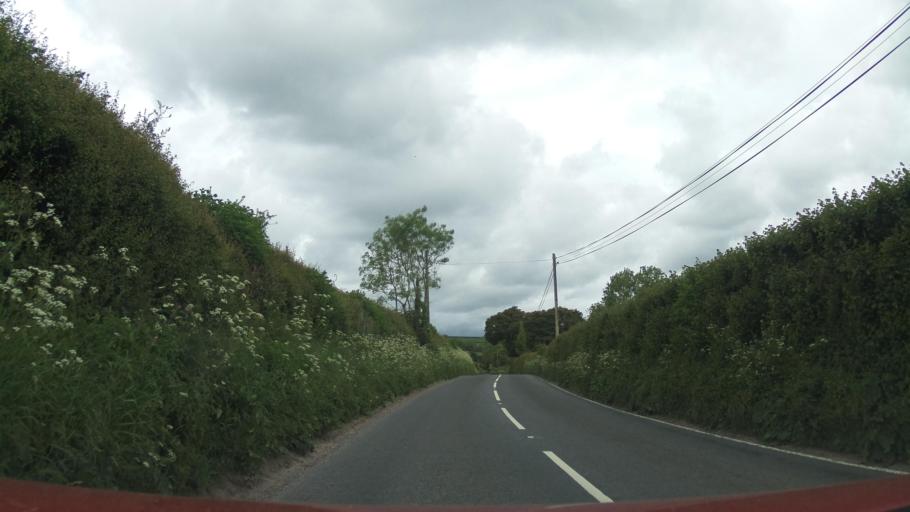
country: GB
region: England
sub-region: Dorset
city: Dorchester
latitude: 50.7492
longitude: -2.4676
